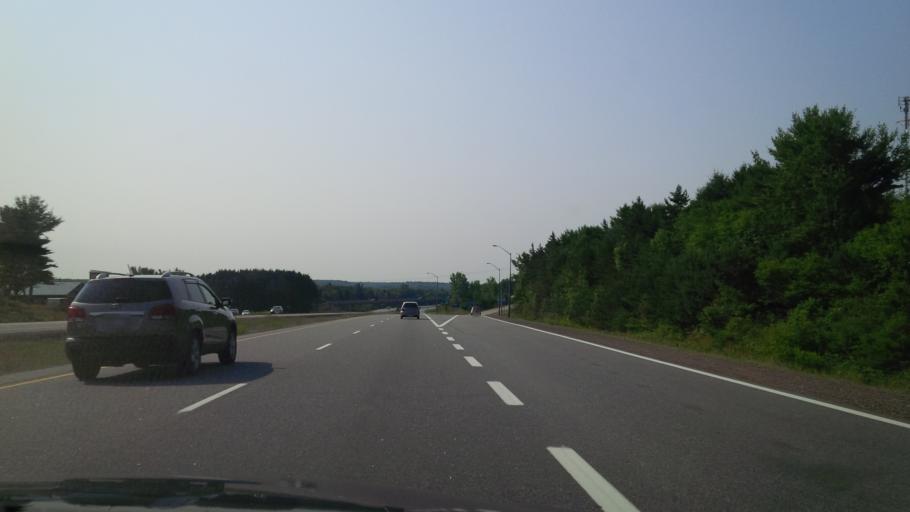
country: CA
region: Ontario
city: Bracebridge
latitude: 45.0570
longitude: -79.2930
